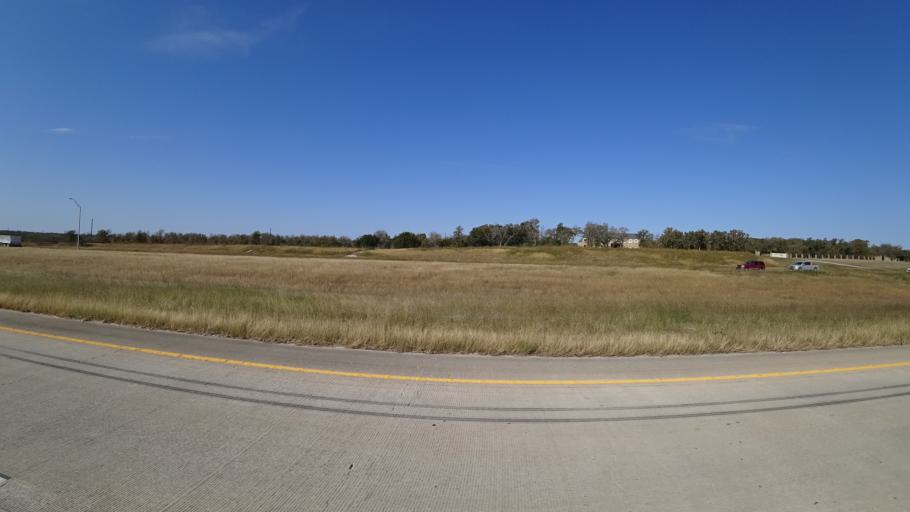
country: US
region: Texas
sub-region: Travis County
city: Hornsby Bend
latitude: 30.2814
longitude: -97.5808
